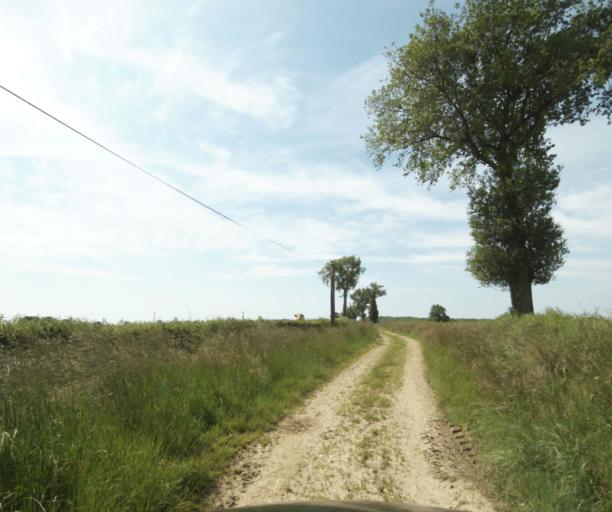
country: FR
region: Bourgogne
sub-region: Departement de Saone-et-Loire
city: Palinges
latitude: 46.5579
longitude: 4.1699
